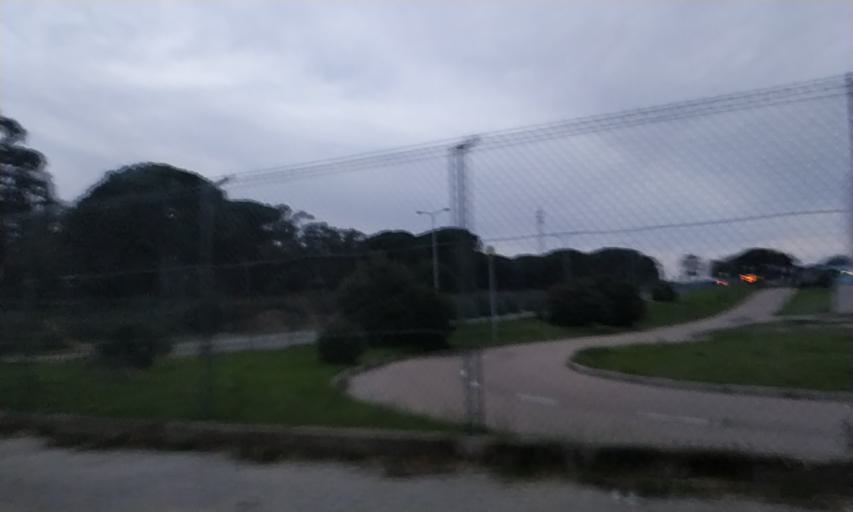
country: PT
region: Setubal
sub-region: Setubal
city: Setubal
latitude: 38.5182
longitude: -8.8504
